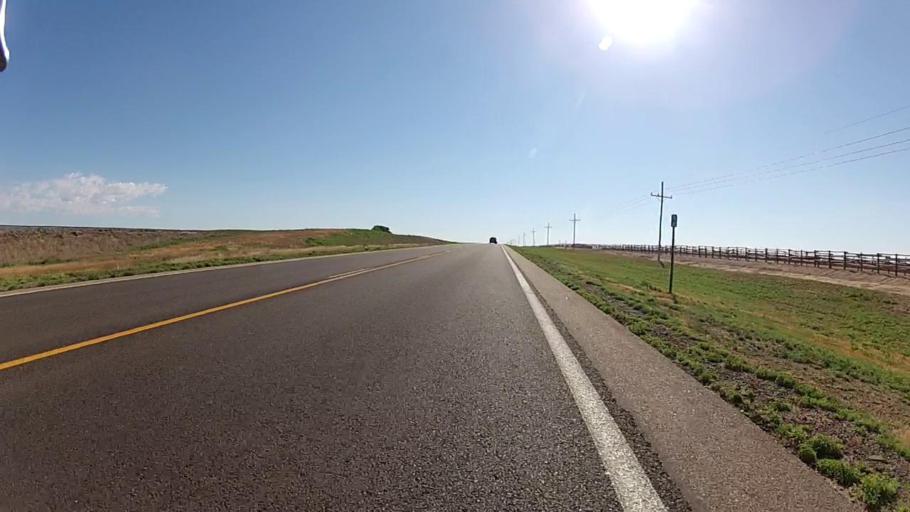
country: US
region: Kansas
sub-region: Haskell County
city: Sublette
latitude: 37.5664
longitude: -100.5516
